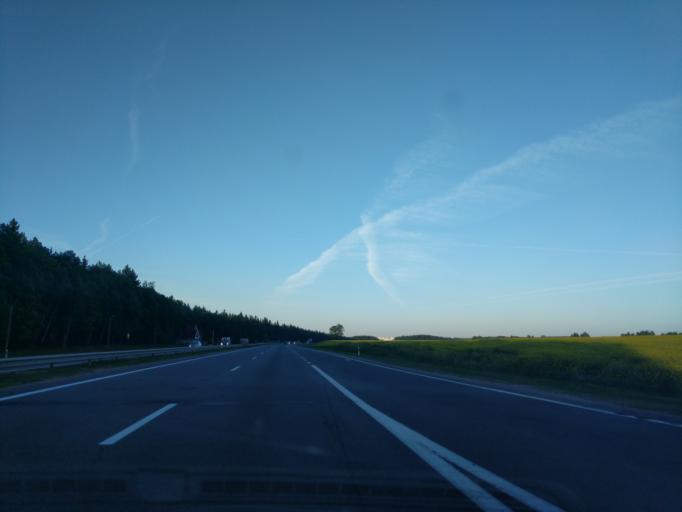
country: BY
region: Minsk
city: Khatsyezhyna
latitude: 53.9181
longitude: 27.2974
